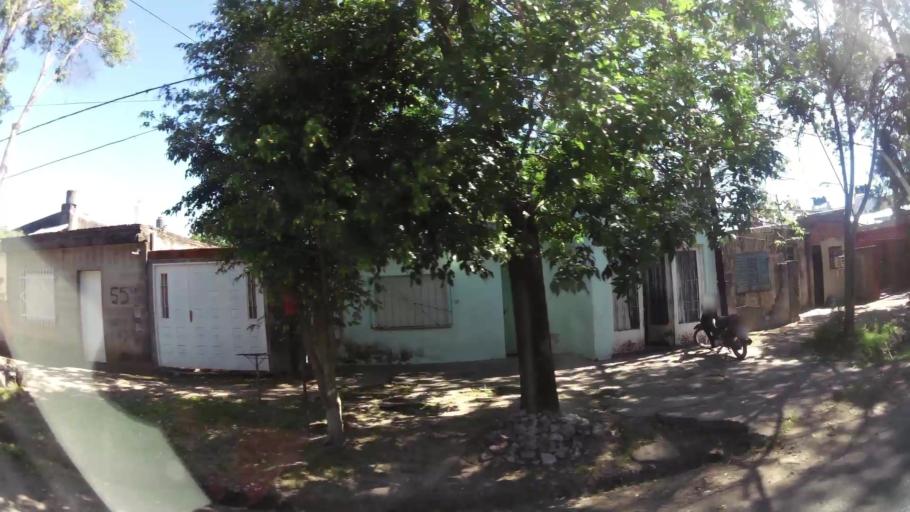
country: AR
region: Santa Fe
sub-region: Departamento de Rosario
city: Rosario
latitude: -32.9683
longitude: -60.6984
